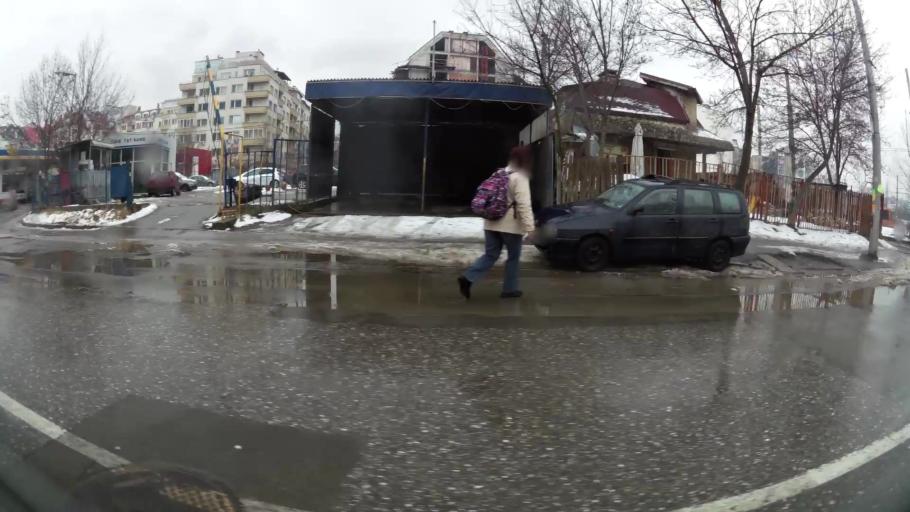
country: BG
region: Sofia-Capital
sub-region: Stolichna Obshtina
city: Sofia
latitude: 42.6602
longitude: 23.2981
